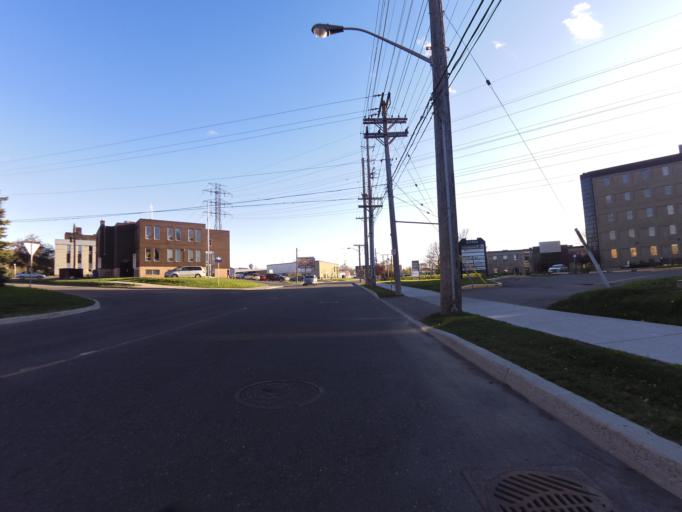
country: CA
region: Ontario
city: Ottawa
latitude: 45.3727
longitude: -75.7497
